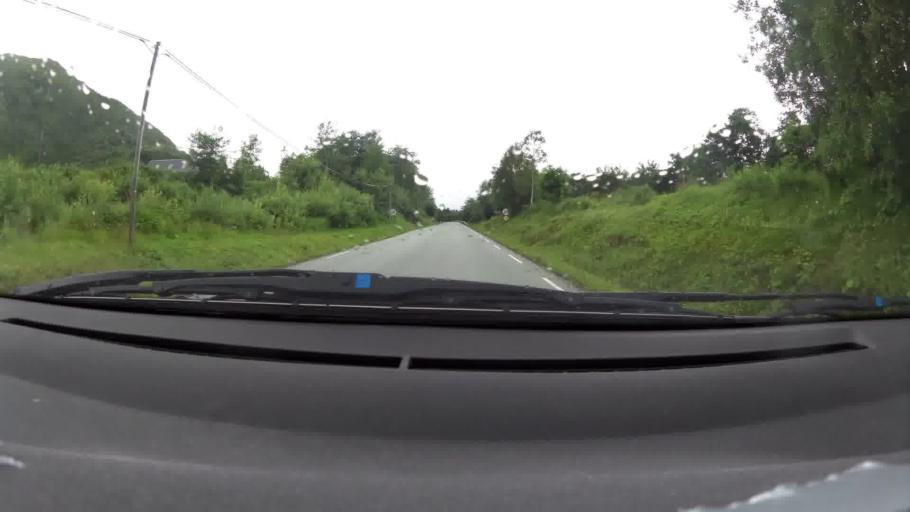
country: NO
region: More og Romsdal
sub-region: Gjemnes
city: Batnfjordsora
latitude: 62.9190
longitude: 7.7530
